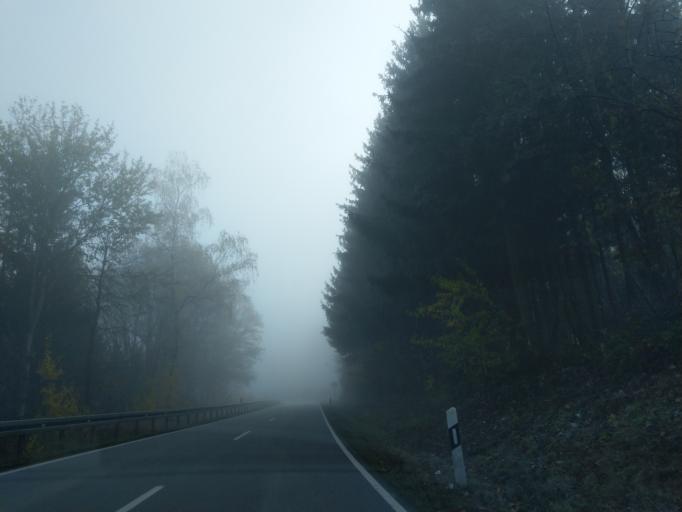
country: DE
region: Bavaria
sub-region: Lower Bavaria
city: Schollnach
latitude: 48.7487
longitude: 13.1669
